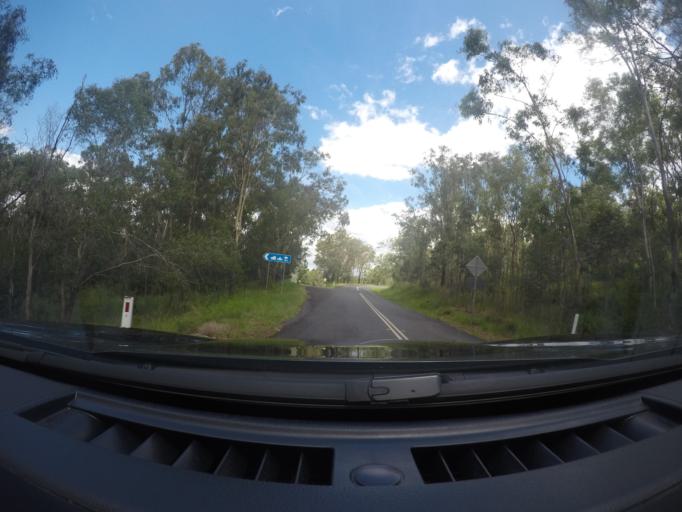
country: AU
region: Queensland
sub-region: Moreton Bay
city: Woodford
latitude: -27.1026
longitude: 152.5594
